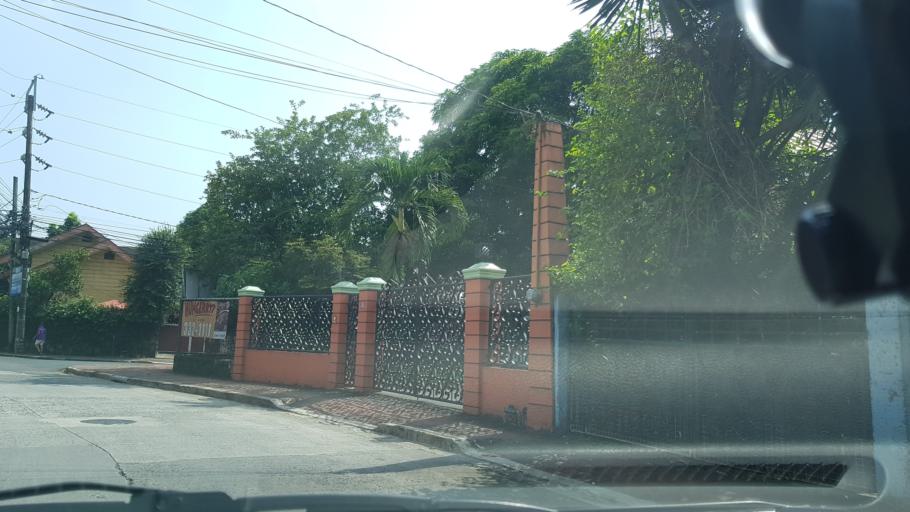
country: PH
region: Calabarzon
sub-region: Province of Rizal
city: San Mateo
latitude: 14.6645
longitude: 121.1116
